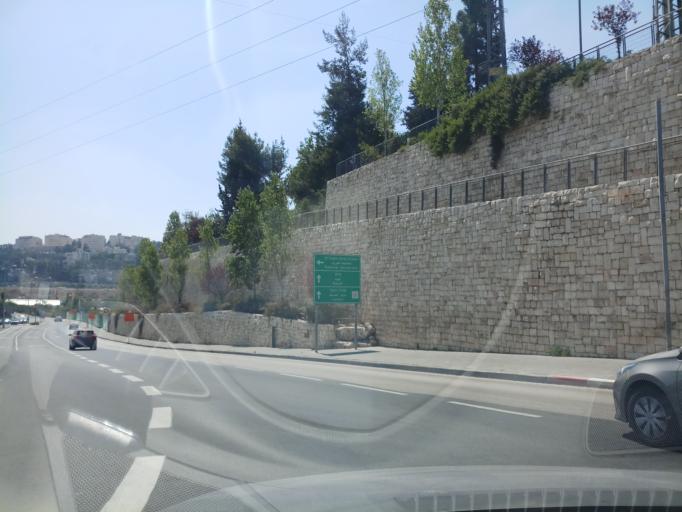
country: IL
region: Jerusalem
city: Jerusalem
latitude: 31.7665
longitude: 35.1957
